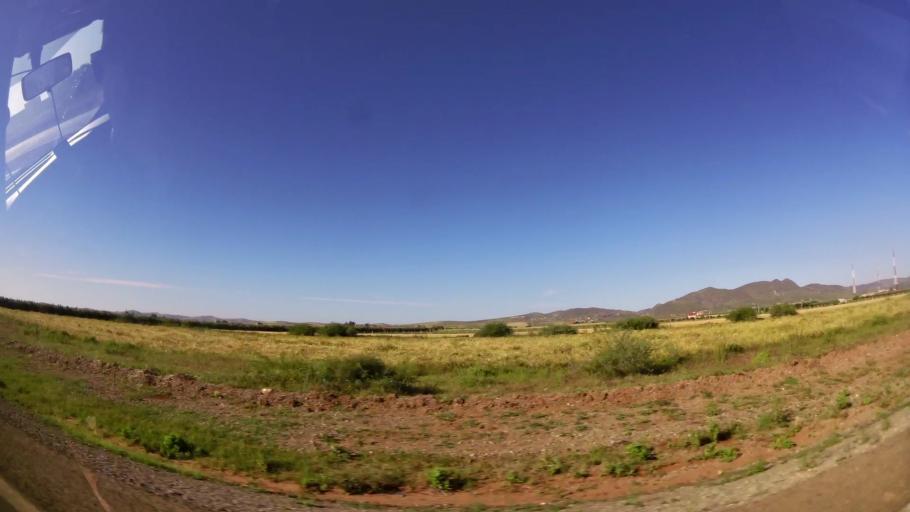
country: MA
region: Oriental
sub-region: Berkane-Taourirt
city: Ahfir
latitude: 34.9886
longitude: -2.1526
